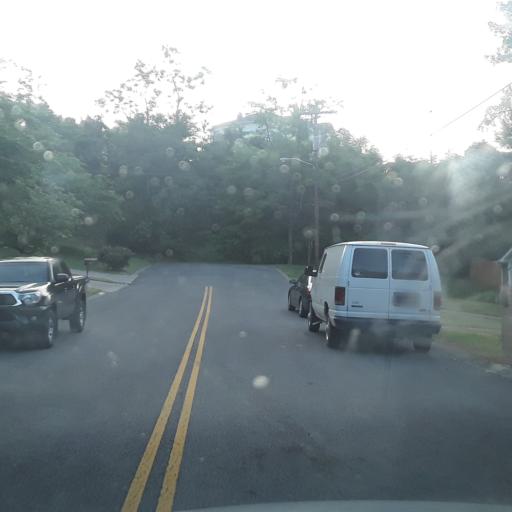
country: US
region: Tennessee
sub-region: Williamson County
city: Brentwood Estates
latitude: 36.0468
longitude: -86.7233
